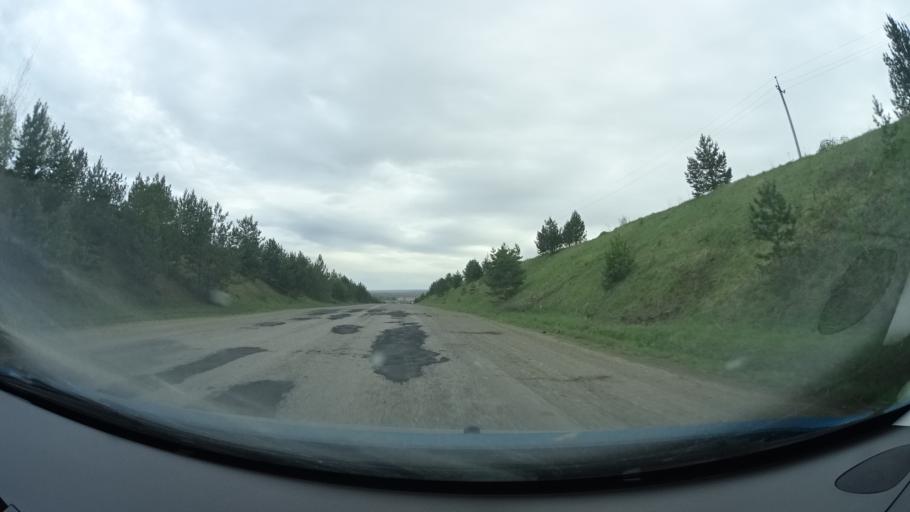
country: RU
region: Perm
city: Osa
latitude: 57.2342
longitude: 55.5940
